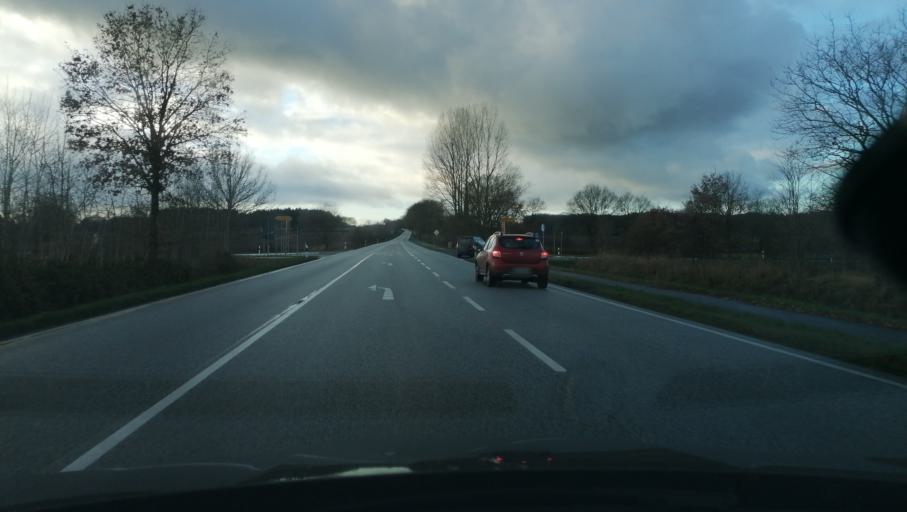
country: DE
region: Schleswig-Holstein
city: Tensbuttel-Rost
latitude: 54.1139
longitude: 9.2440
